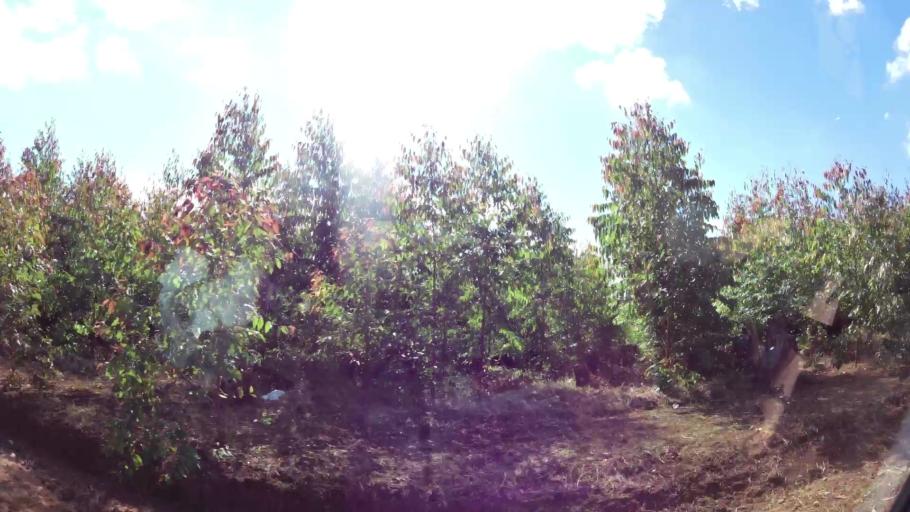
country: ZA
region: Limpopo
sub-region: Mopani District Municipality
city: Tzaneen
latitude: -23.8078
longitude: 30.1689
